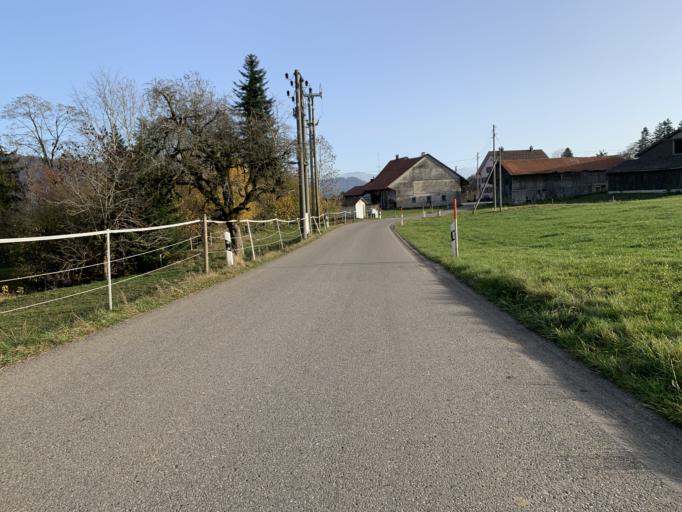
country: CH
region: Zurich
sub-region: Bezirk Hinwil
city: Wald
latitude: 47.3108
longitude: 8.9008
